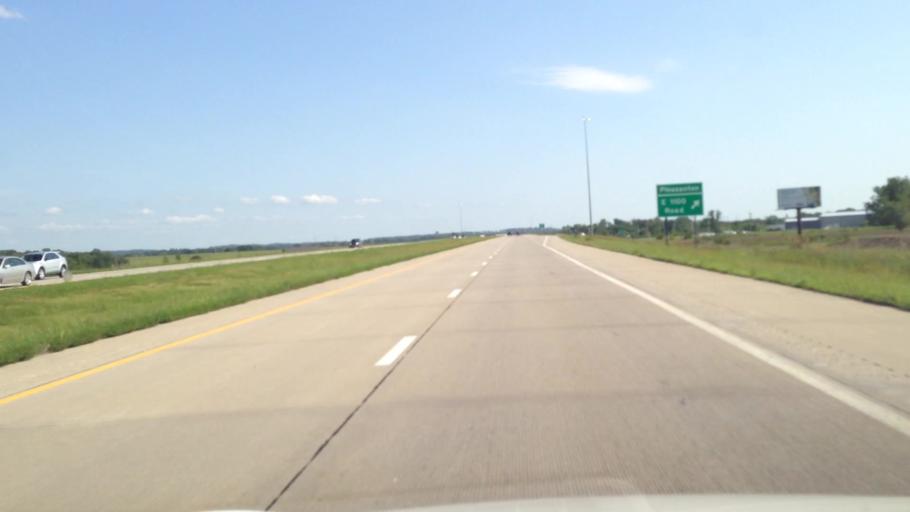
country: US
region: Kansas
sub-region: Linn County
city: Pleasanton
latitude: 38.1870
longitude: -94.7027
